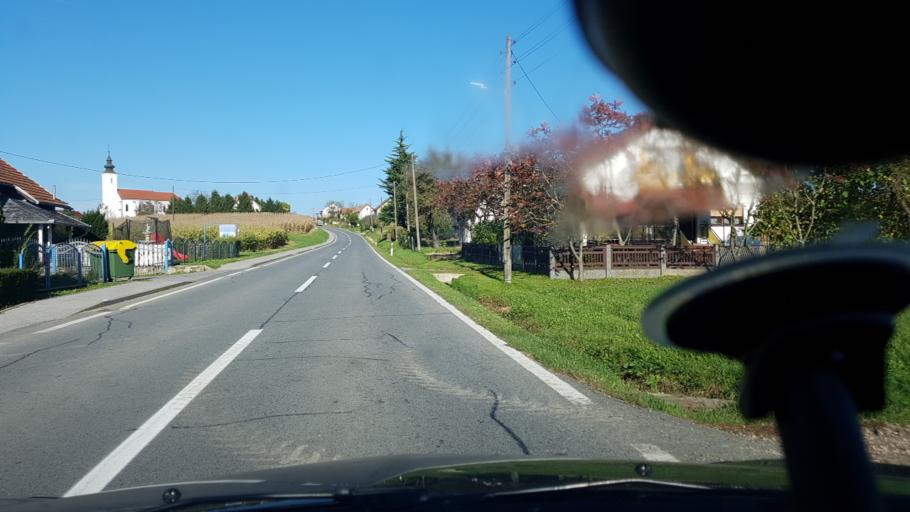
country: HR
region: Bjelovarsko-Bilogorska
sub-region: Grad Cazma
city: Cazma
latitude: 45.7815
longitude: 16.6436
